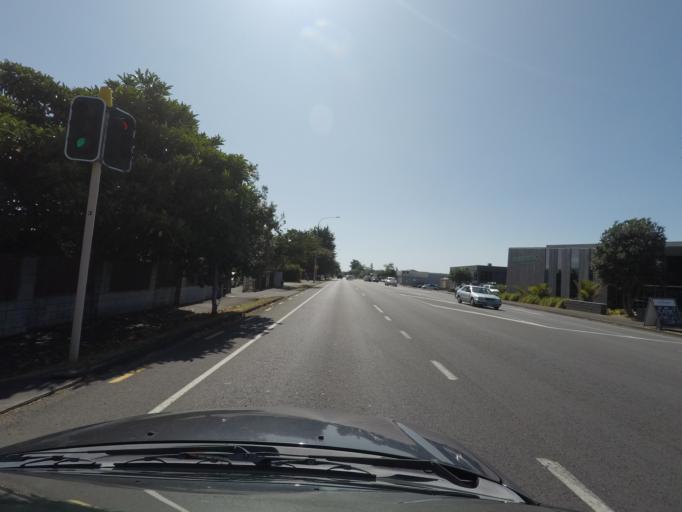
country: NZ
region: Auckland
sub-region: Auckland
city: Rosebank
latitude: -36.8841
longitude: 174.6822
